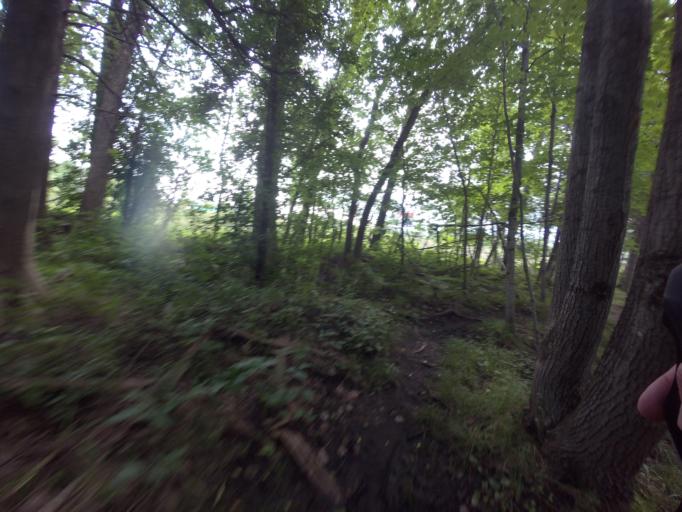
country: CA
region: Ontario
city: Bells Corners
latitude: 45.0329
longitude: -75.6630
